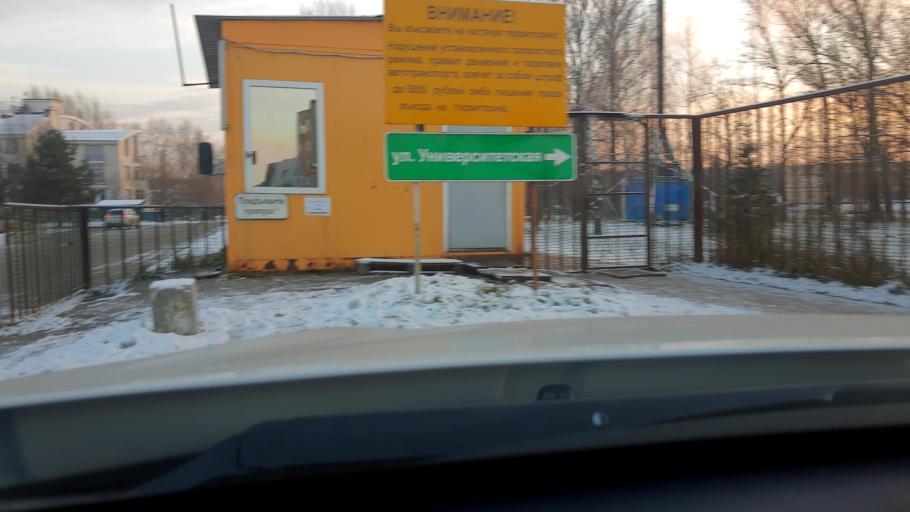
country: RU
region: Moskovskaya
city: Zarech'ye
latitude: 55.6777
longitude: 37.3893
